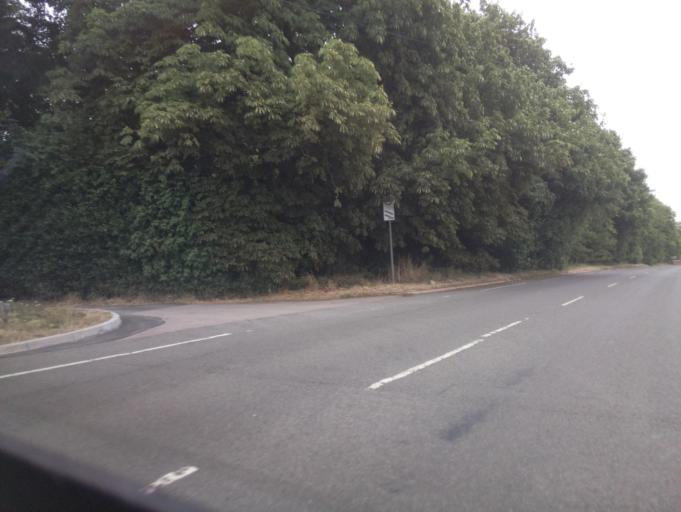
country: GB
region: England
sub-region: Derbyshire
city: Ilkeston
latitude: 52.9172
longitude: -1.3266
